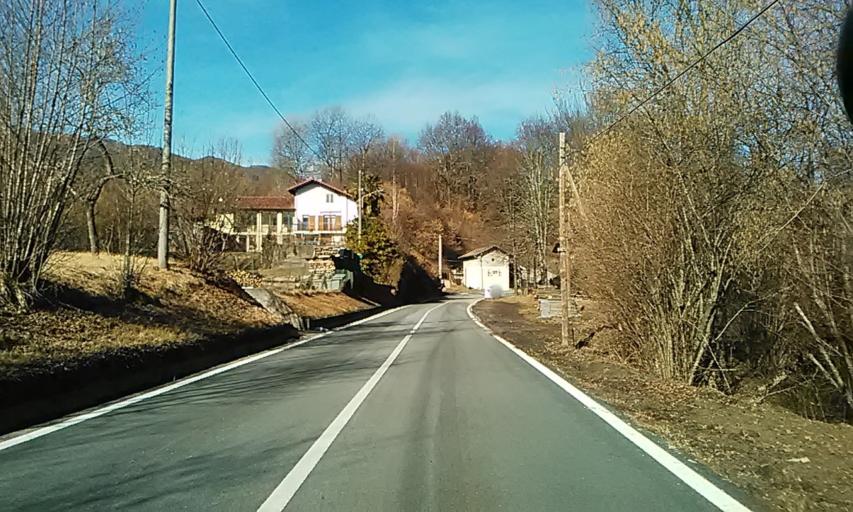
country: IT
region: Piedmont
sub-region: Provincia di Vercelli
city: Cellio
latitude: 45.7399
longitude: 8.3039
